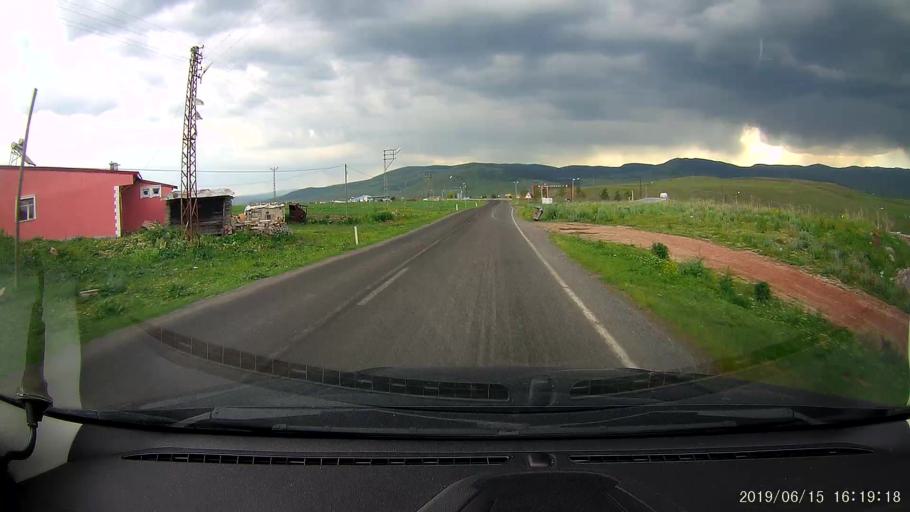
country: TR
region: Ardahan
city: Hanak
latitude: 41.2295
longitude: 42.8504
